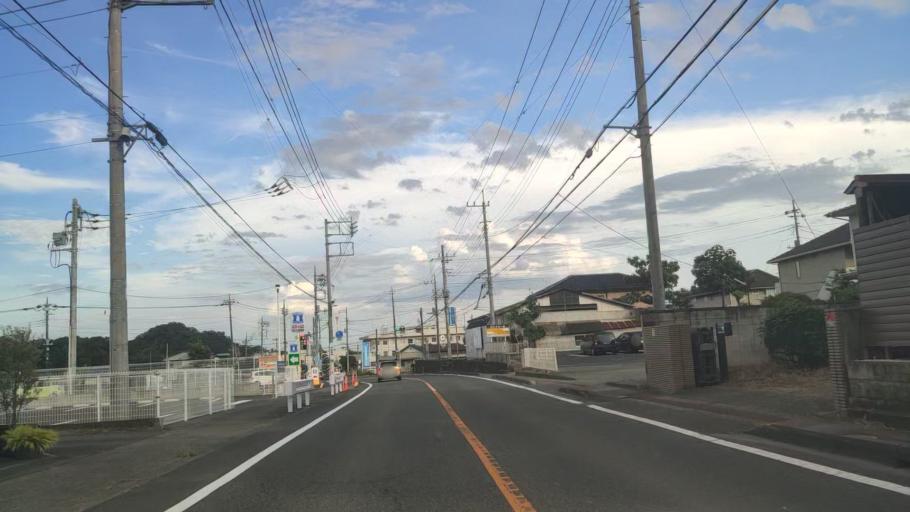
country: JP
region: Gunma
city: Kiryu
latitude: 36.4177
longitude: 139.3084
